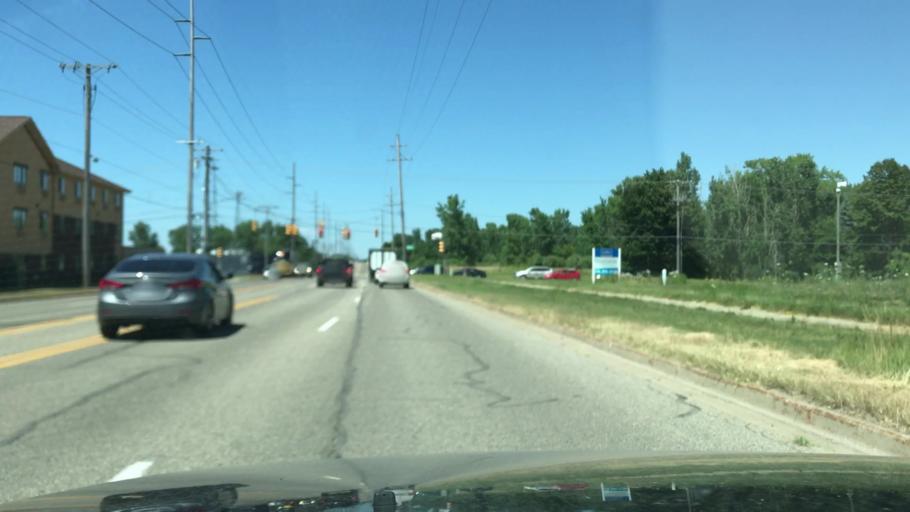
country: US
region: Michigan
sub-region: Ottawa County
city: Holland
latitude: 42.7751
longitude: -86.0774
